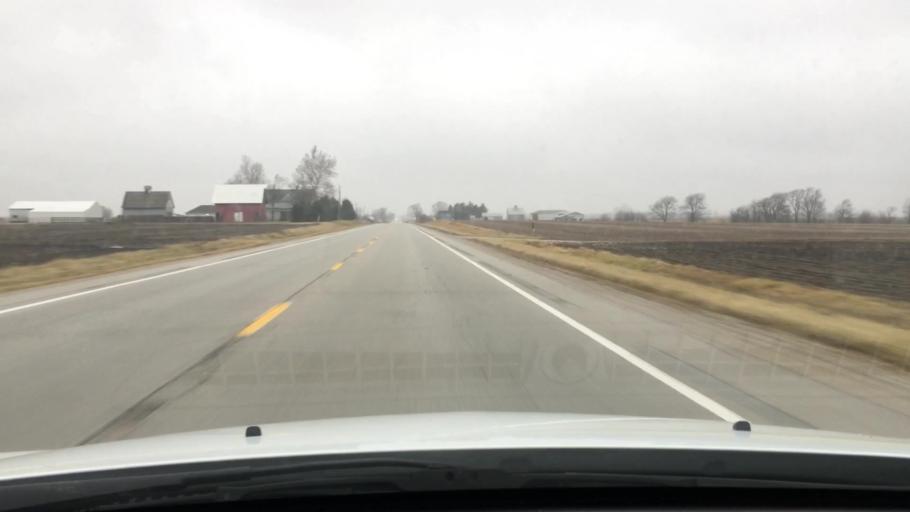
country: US
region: Illinois
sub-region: Livingston County
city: Pontiac
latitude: 40.8727
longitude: -88.7383
